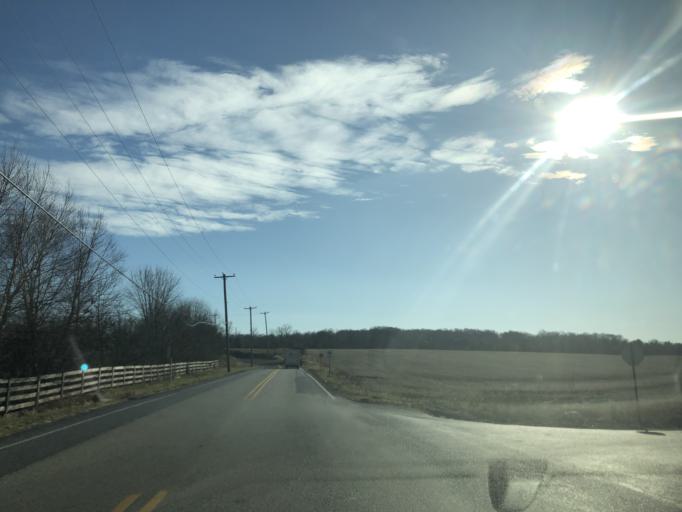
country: US
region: Pennsylvania
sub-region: Chester County
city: Toughkenamon
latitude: 39.8548
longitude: -75.7712
